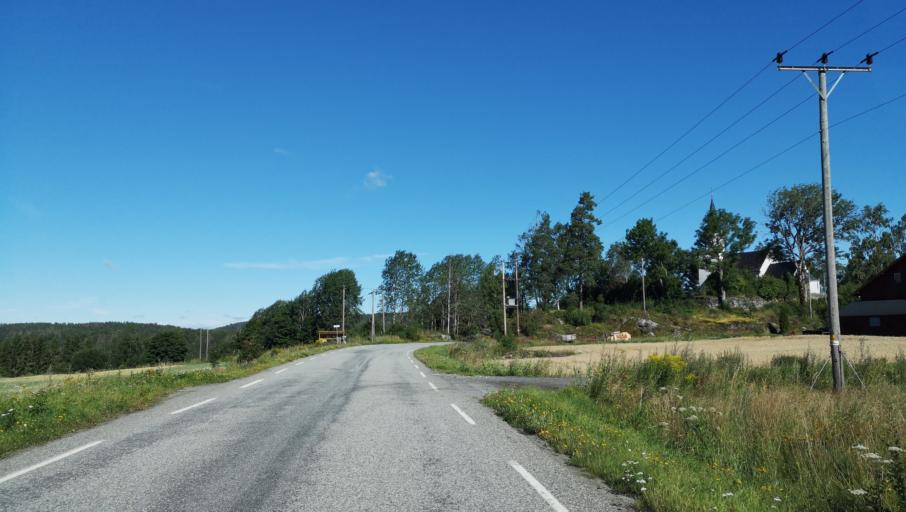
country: NO
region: Ostfold
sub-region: Hobol
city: Tomter
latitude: 59.6501
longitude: 11.0119
